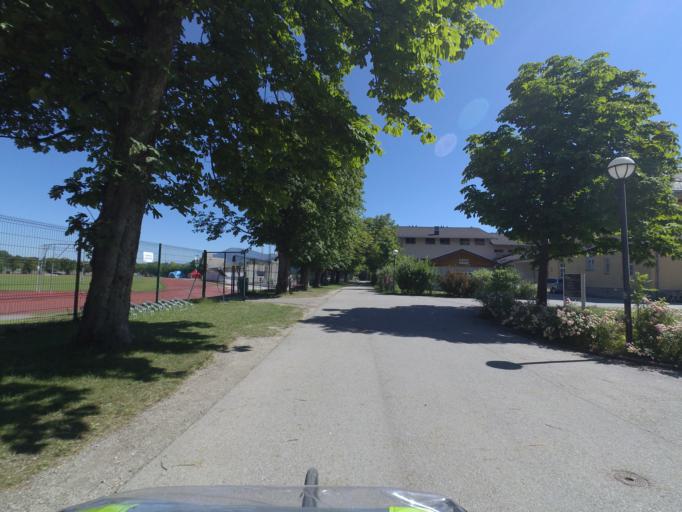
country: AT
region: Salzburg
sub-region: Politischer Bezirk Hallein
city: Puch bei Hallein
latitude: 47.7207
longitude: 13.0693
